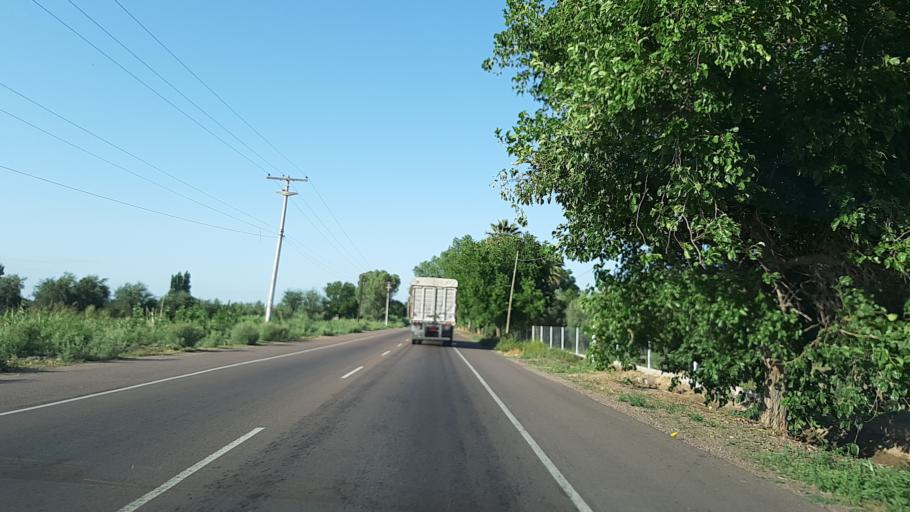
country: AR
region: Mendoza
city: San Martin
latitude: -33.0325
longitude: -68.5119
